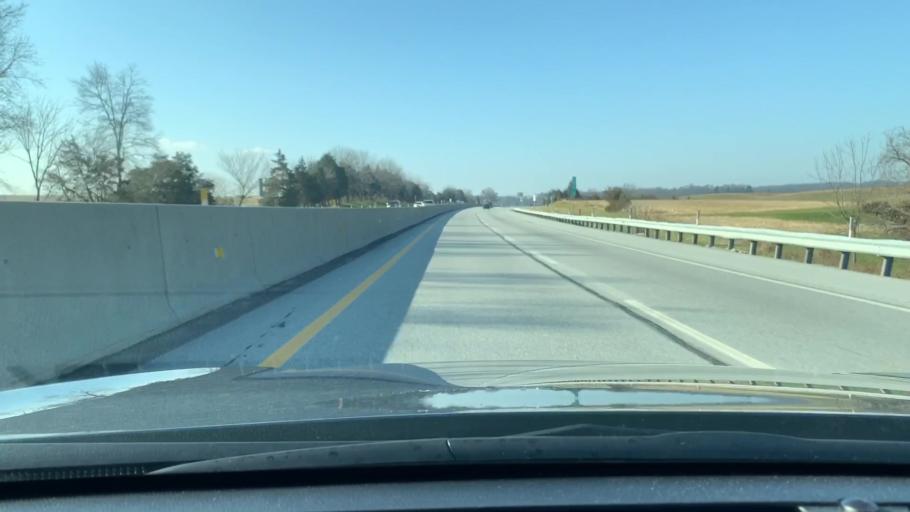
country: US
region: Pennsylvania
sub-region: Lancaster County
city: Elizabethtown
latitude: 40.2074
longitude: -76.5979
